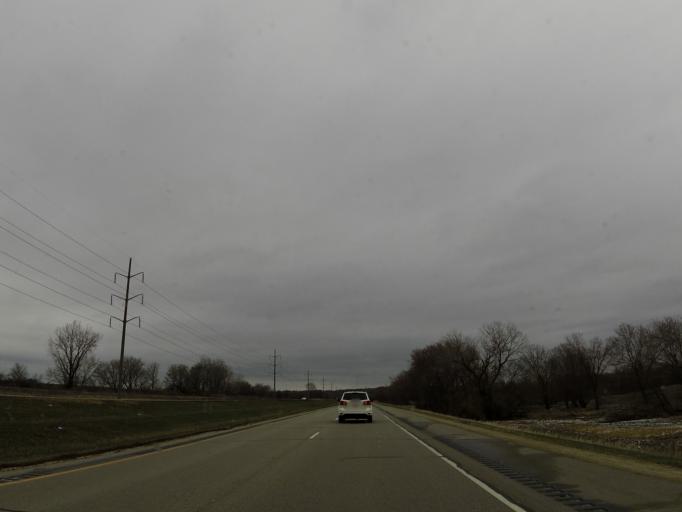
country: US
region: Minnesota
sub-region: Olmsted County
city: Byron
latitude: 44.0283
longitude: -92.5878
